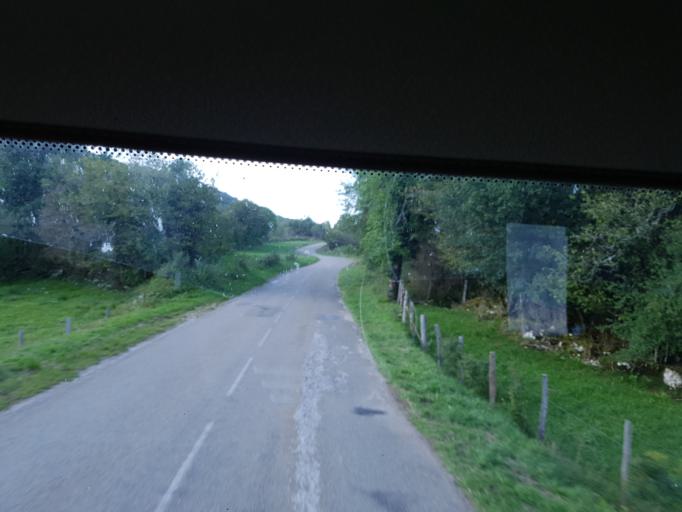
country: FR
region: Franche-Comte
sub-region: Departement du Jura
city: Moirans-en-Montagne
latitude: 46.4074
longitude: 5.6484
